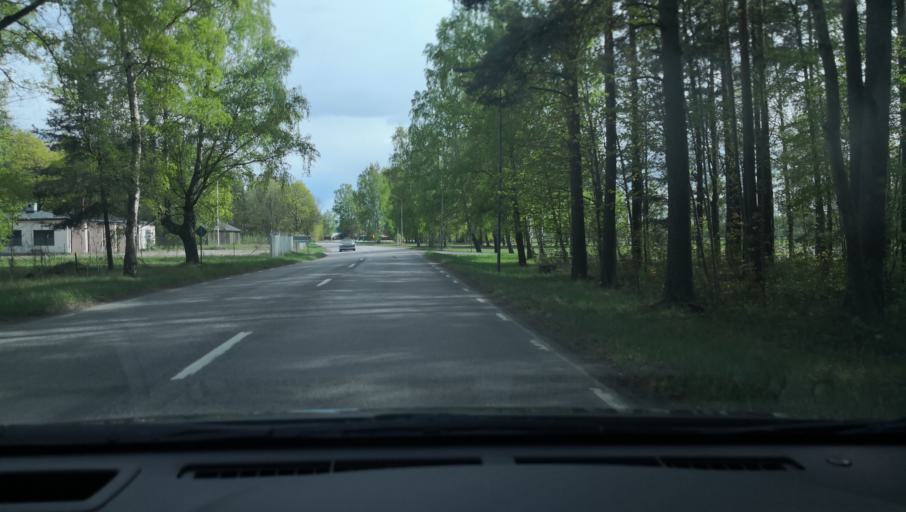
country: SE
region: OErebro
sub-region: Kumla Kommun
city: Kumla
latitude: 59.0899
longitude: 15.1584
